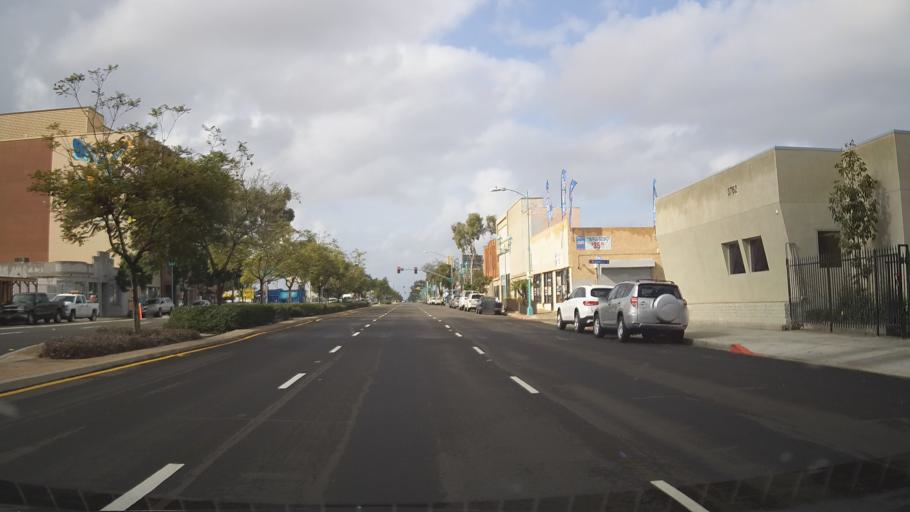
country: US
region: California
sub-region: San Diego County
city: San Diego
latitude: 32.7553
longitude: -117.1121
